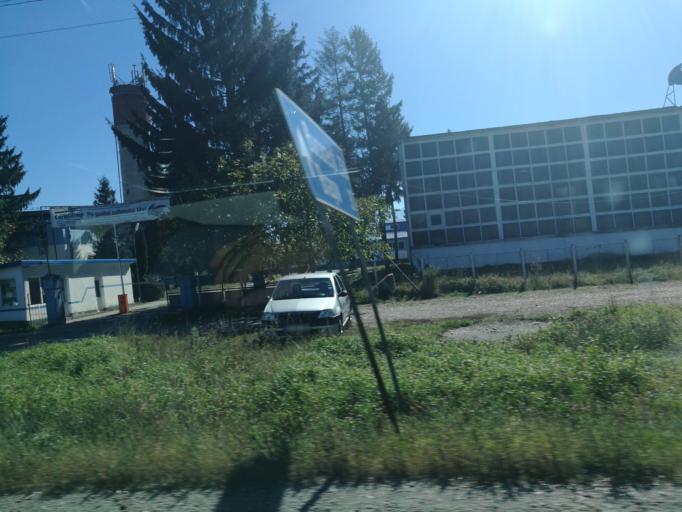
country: RO
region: Brasov
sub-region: Comuna Ucea de Jos
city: Ucea de Jos
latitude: 45.7884
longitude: 24.6751
